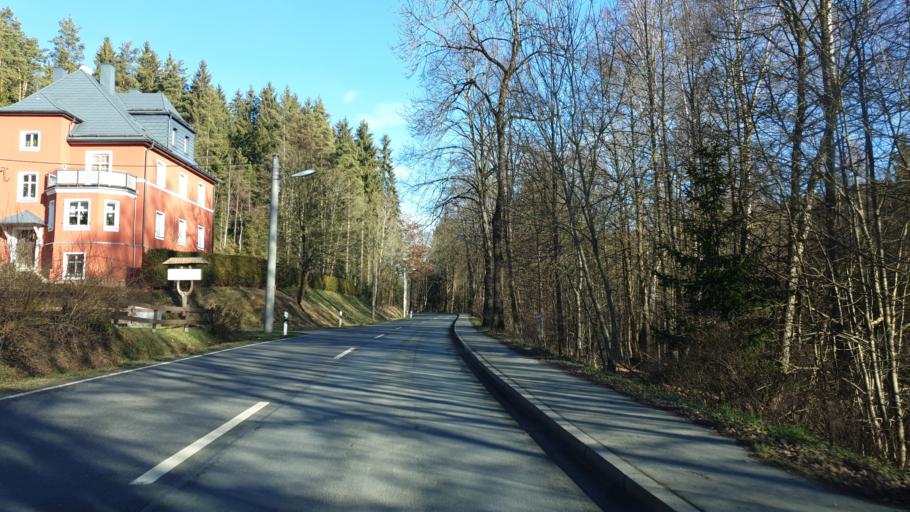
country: DE
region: Saxony
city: Bad Elster
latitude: 50.2933
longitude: 12.2448
